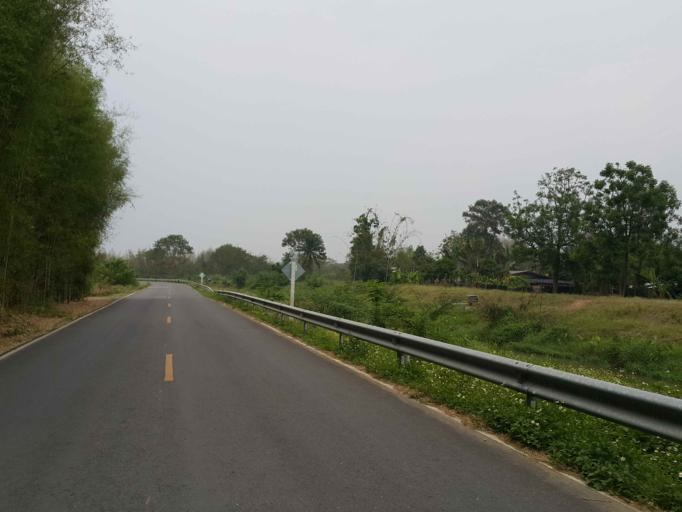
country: TH
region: Chiang Mai
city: San Sai
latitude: 18.9398
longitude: 98.9952
